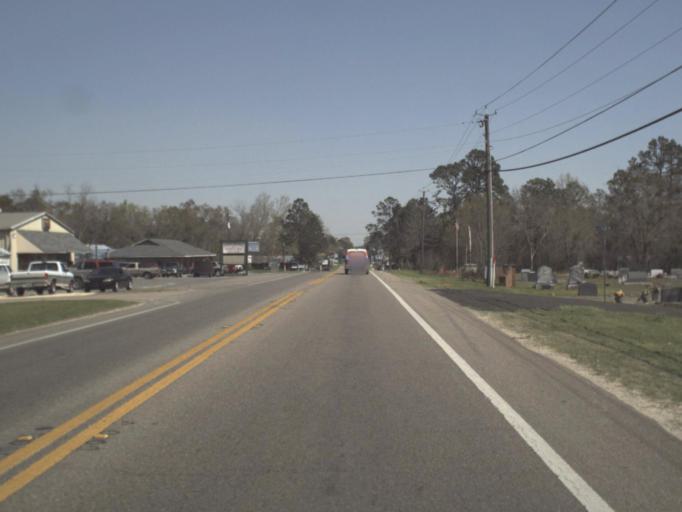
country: US
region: Florida
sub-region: Calhoun County
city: Blountstown
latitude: 30.4438
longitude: -85.0630
